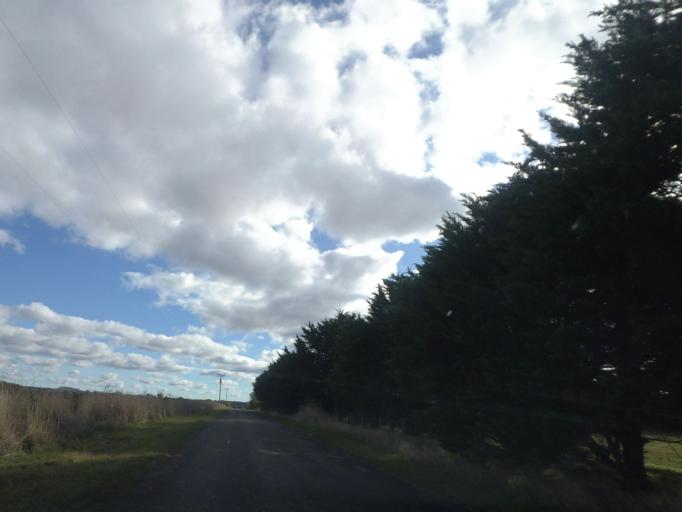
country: AU
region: Victoria
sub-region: Mount Alexander
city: Castlemaine
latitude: -37.2511
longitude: 144.4000
